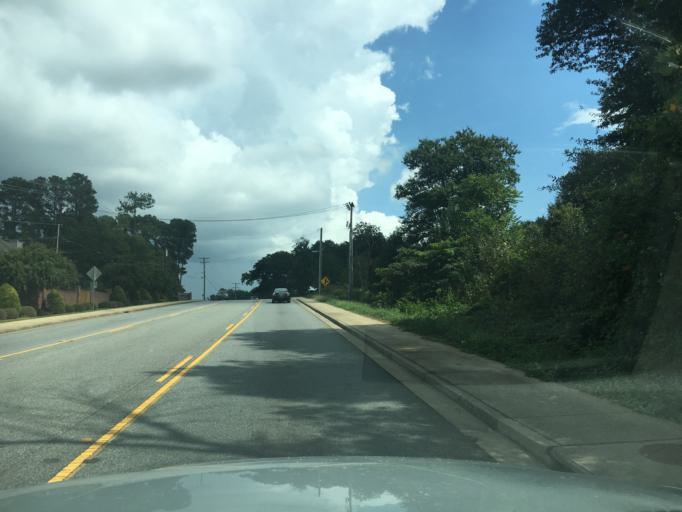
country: US
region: South Carolina
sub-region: Greenville County
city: Taylors
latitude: 34.8909
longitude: -82.2793
